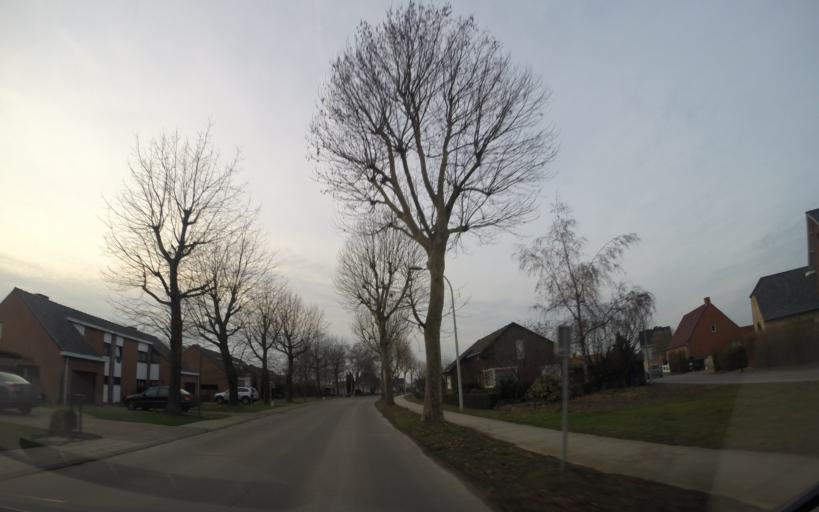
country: BE
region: Flanders
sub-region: Provincie Oost-Vlaanderen
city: Deinze
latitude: 51.0084
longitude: 3.4744
